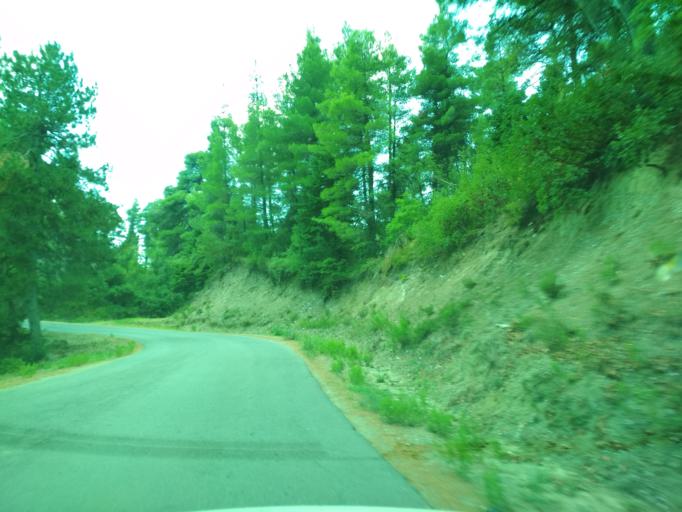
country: GR
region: Central Greece
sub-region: Nomos Evvoias
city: Roviai
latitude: 38.8554
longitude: 23.2874
